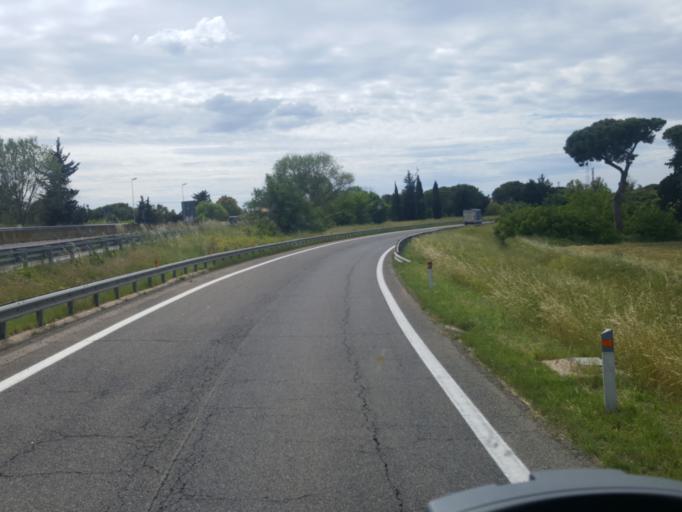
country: IT
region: Latium
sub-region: Citta metropolitana di Roma Capitale
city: Ara Nova
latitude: 41.9131
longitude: 12.2169
